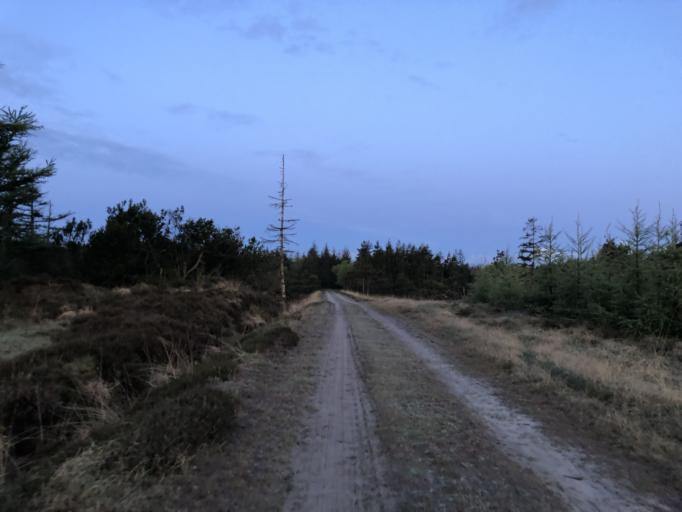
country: DK
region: Central Jutland
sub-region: Holstebro Kommune
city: Ulfborg
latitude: 56.2647
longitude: 8.3975
